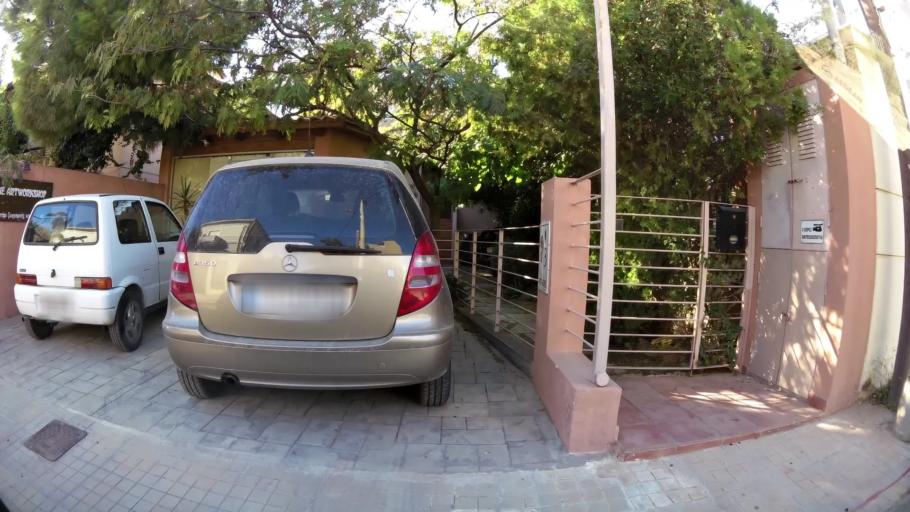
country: GR
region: Attica
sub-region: Nomarchia Anatolikis Attikis
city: Vari
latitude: 37.8340
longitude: 23.8122
